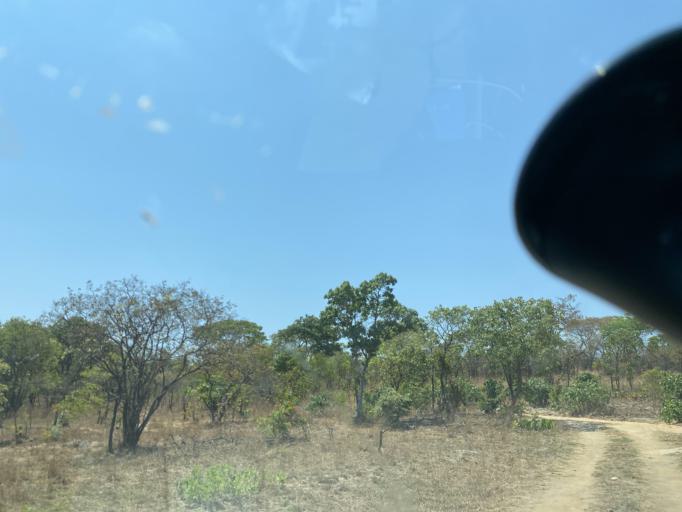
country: ZM
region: Lusaka
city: Chongwe
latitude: -15.4358
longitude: 29.1972
